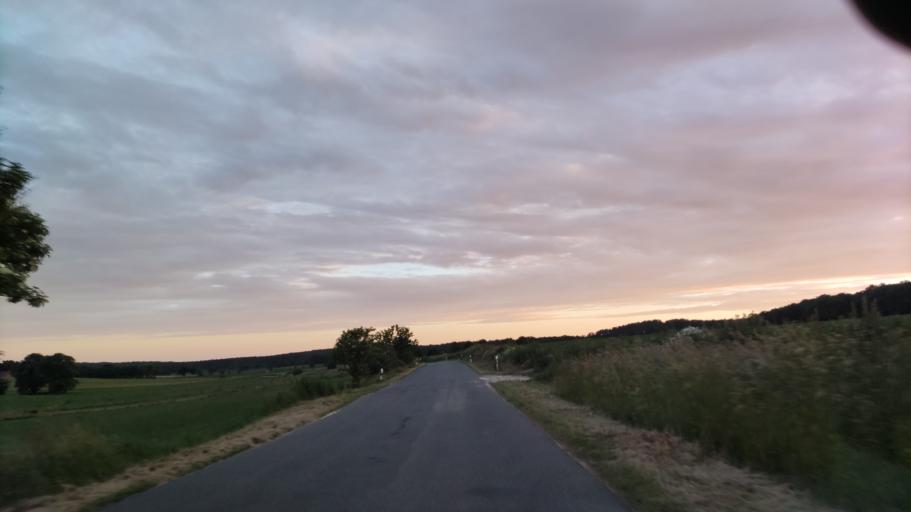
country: DE
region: Lower Saxony
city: Neu Darchau
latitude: 53.1955
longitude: 10.9383
